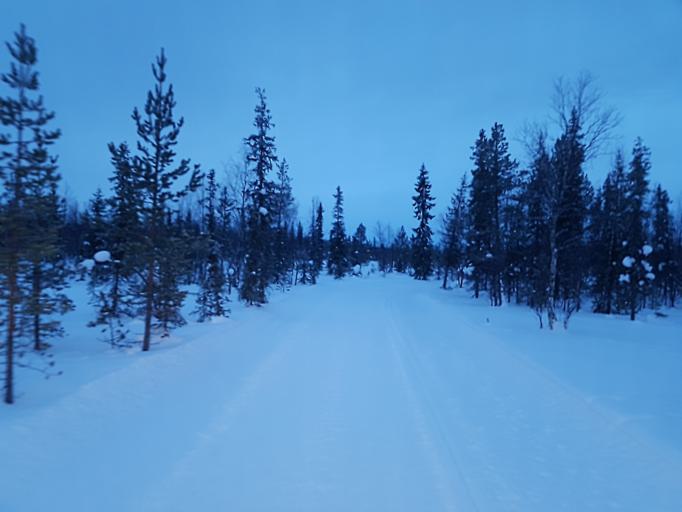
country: FI
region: Lapland
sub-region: Tunturi-Lappi
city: Kolari
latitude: 67.6162
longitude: 24.1673
